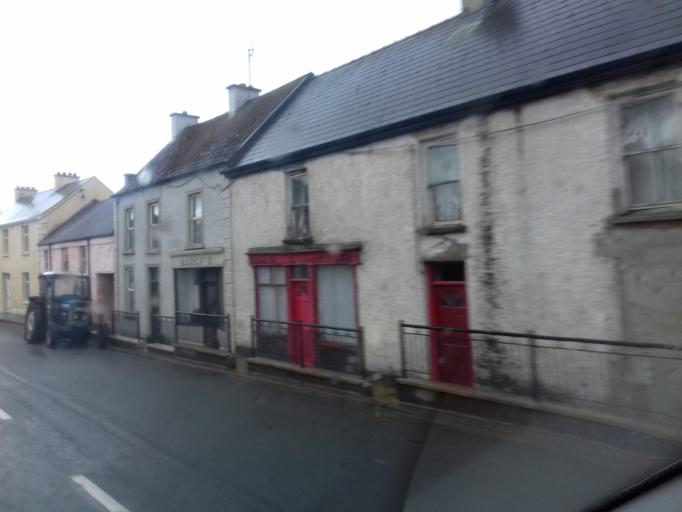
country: IE
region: Ulster
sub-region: An Cabhan
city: Ballyconnell
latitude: 54.1212
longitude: -7.6768
